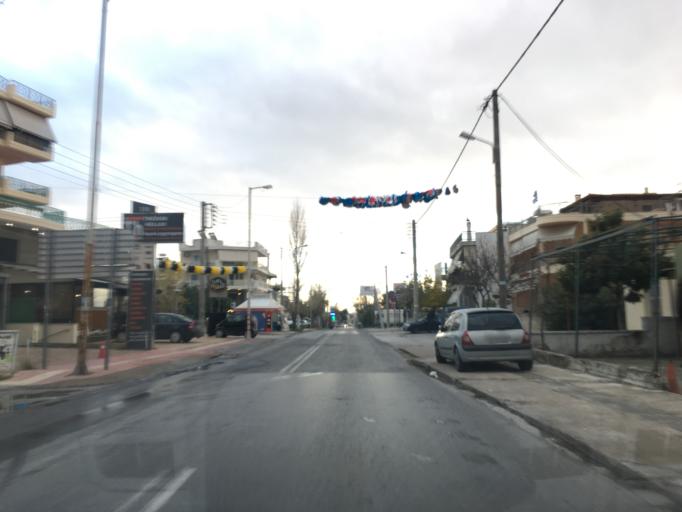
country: GR
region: Attica
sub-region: Nomarchia Athinas
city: Nea Filadelfeia
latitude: 38.0518
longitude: 23.7299
